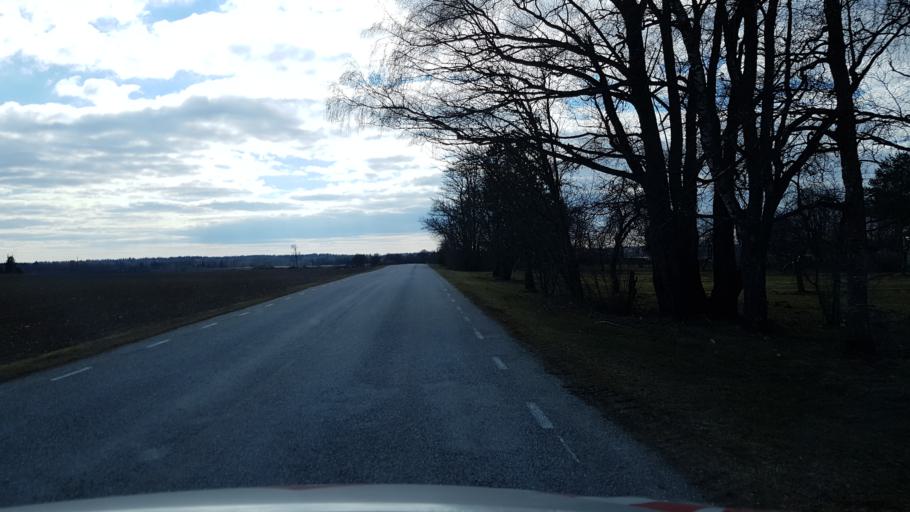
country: EE
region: Laeaene-Virumaa
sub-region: Kadrina vald
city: Kadrina
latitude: 59.2928
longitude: 26.2022
